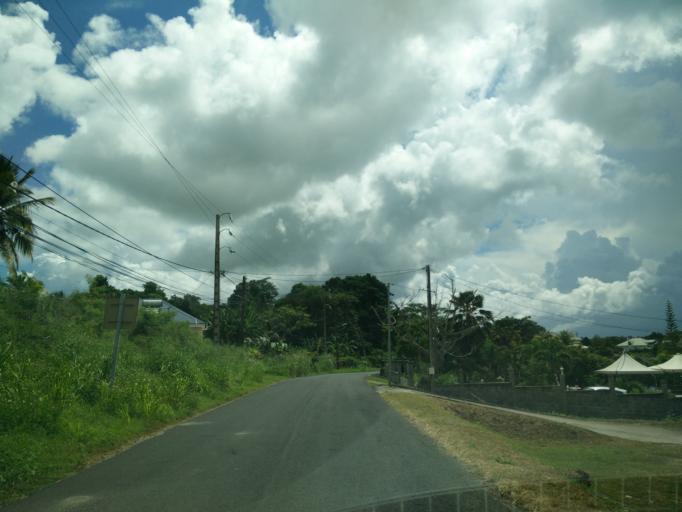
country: GP
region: Guadeloupe
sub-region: Guadeloupe
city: Le Moule
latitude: 16.2721
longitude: -61.3336
